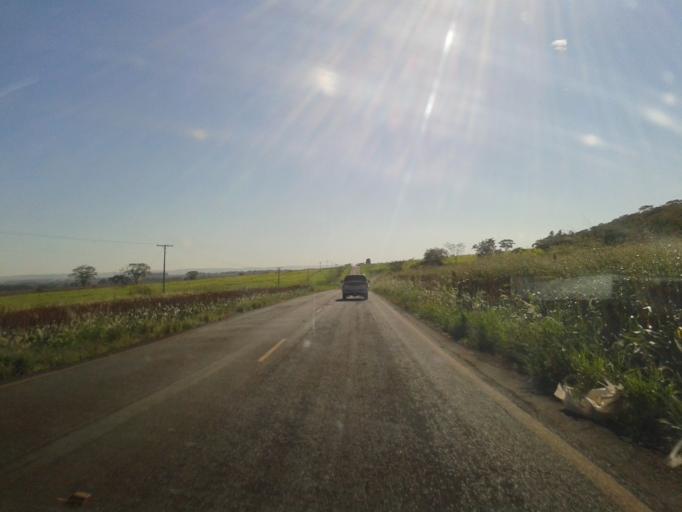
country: BR
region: Minas Gerais
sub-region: Capinopolis
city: Capinopolis
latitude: -18.6263
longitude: -49.5369
